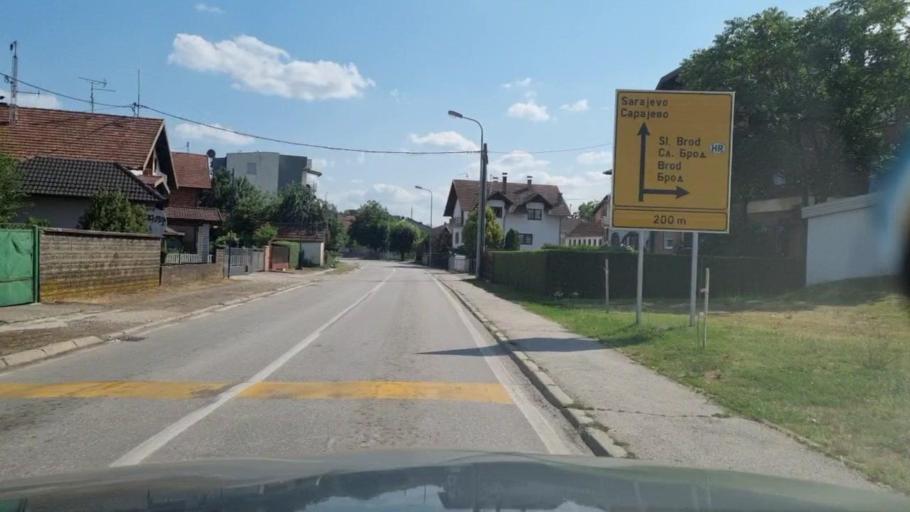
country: BA
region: Federation of Bosnia and Herzegovina
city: Odzak
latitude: 45.0164
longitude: 18.3287
